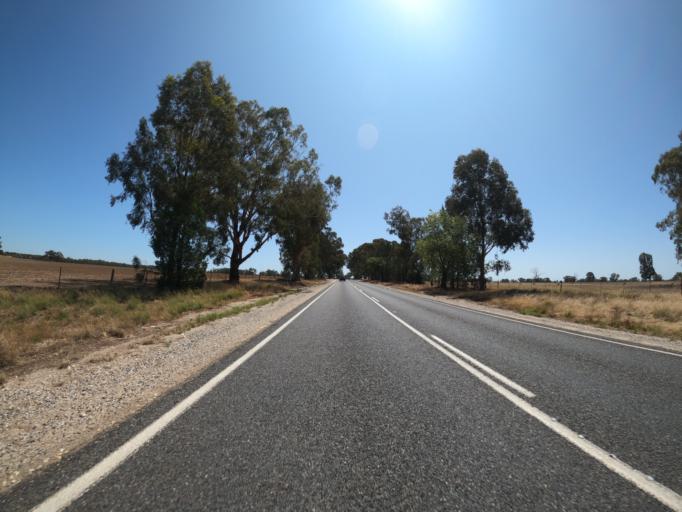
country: AU
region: New South Wales
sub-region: Corowa Shire
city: Corowa
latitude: -36.0733
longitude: 146.2335
